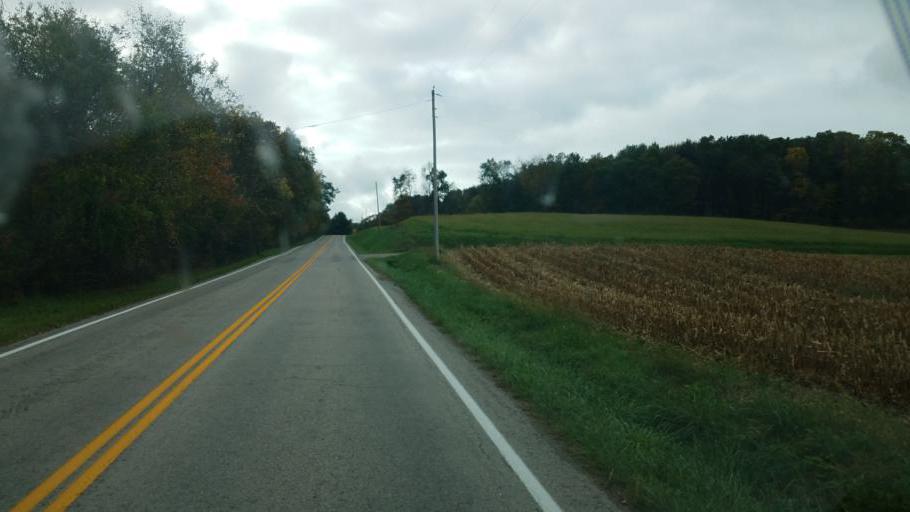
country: US
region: Ohio
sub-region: Ashland County
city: Loudonville
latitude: 40.6441
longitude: -82.3003
